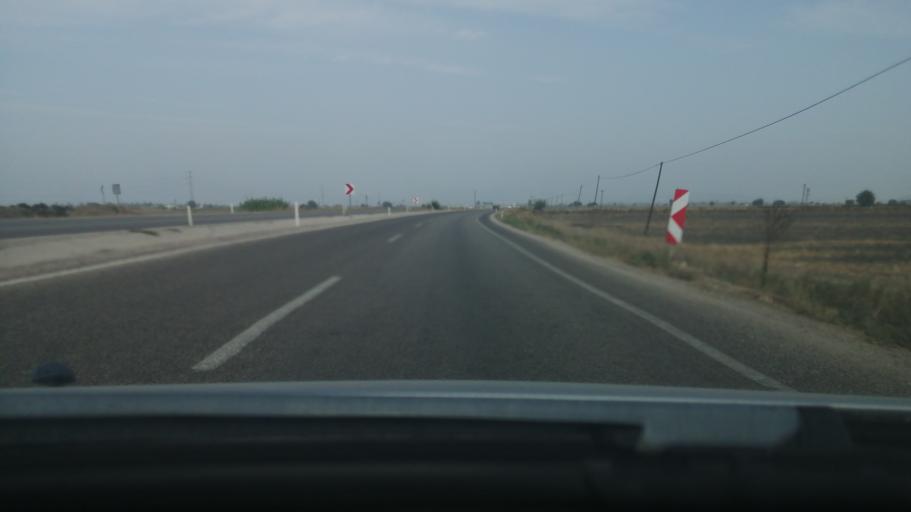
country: TR
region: Adana
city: Imamoglu
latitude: 37.3059
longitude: 35.7187
